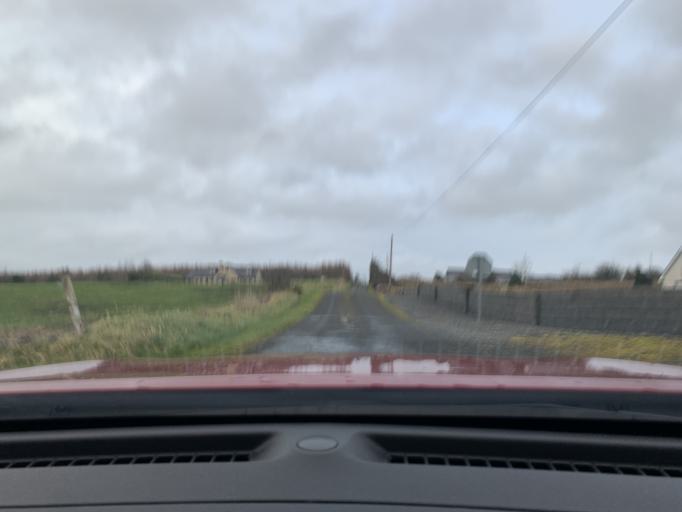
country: IE
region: Connaught
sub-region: Roscommon
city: Boyle
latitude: 53.9824
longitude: -8.4229
